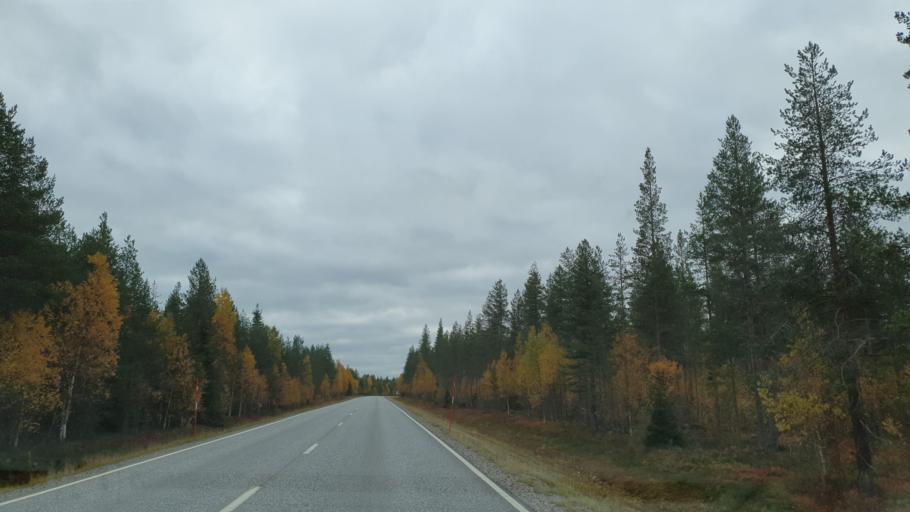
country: FI
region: Lapland
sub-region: Rovaniemi
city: Rovaniemi
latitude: 66.4001
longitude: 25.8551
